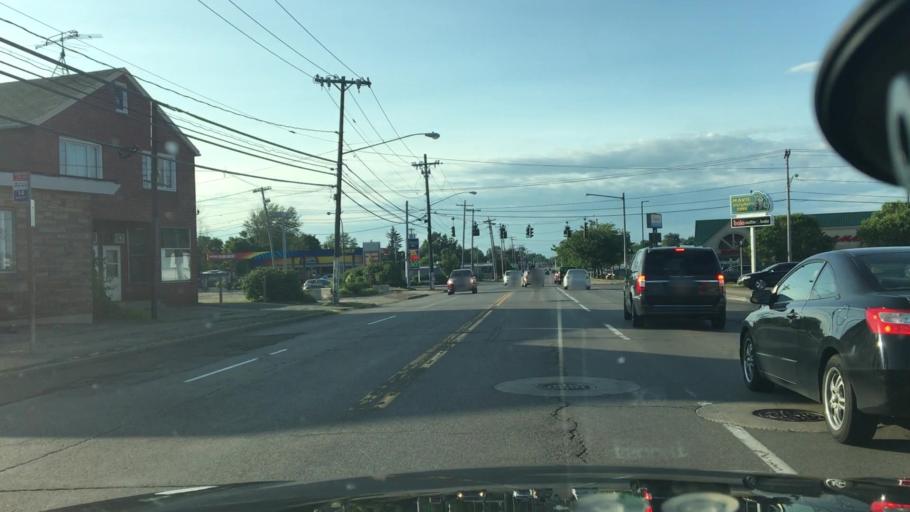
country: US
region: New York
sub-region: Erie County
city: Lackawanna
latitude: 42.8274
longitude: -78.8041
